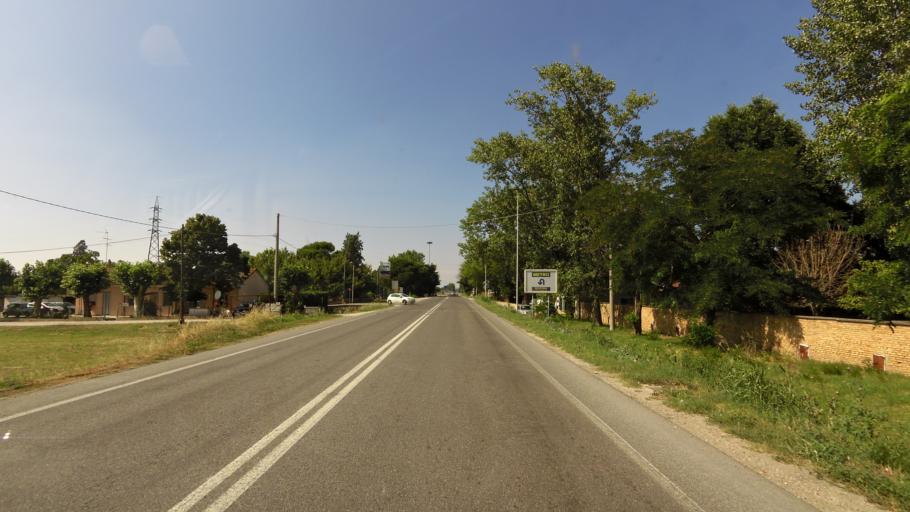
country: IT
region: Emilia-Romagna
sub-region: Provincia di Ravenna
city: Ravenna
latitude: 44.4444
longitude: 12.2106
